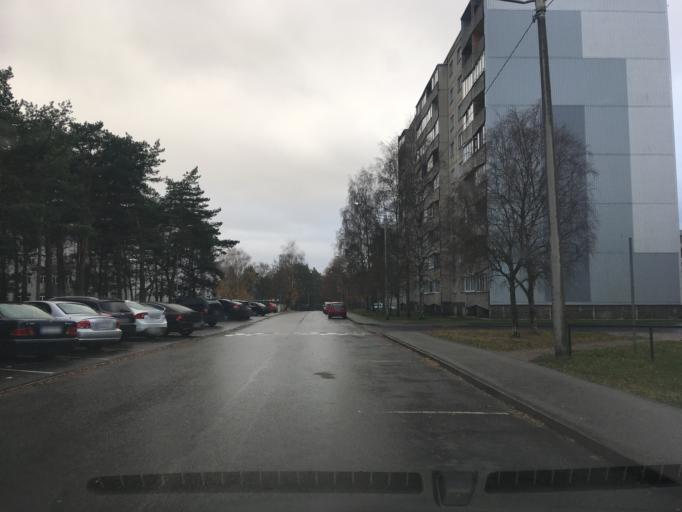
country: EE
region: Harju
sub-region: Tallinna linn
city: Tallinn
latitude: 59.3757
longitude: 24.7122
